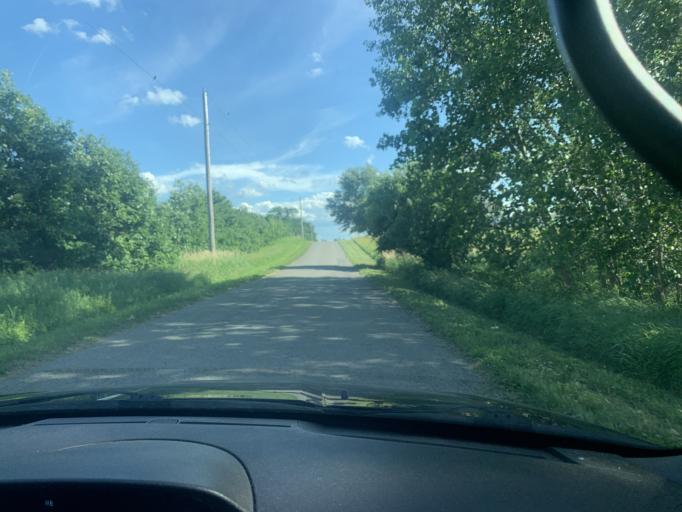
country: US
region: Ohio
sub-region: Logan County
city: De Graff
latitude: 40.3056
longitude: -83.8749
